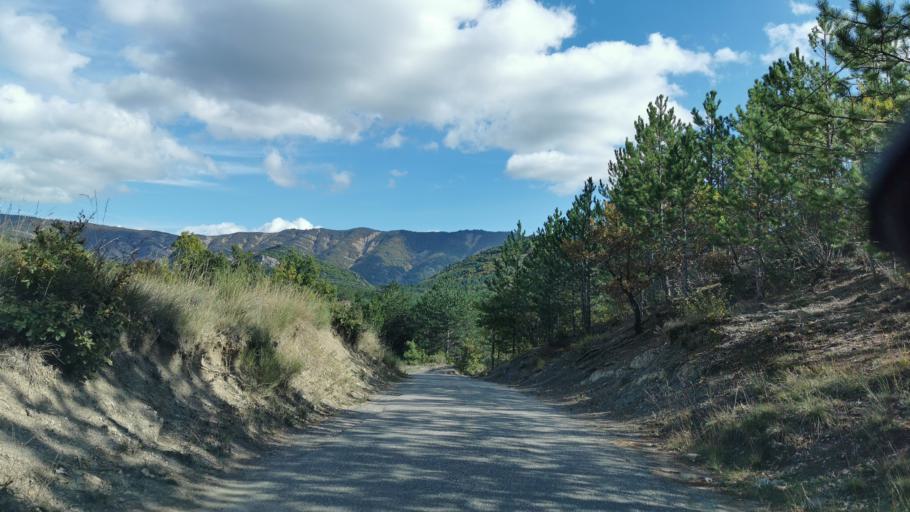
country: FR
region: Provence-Alpes-Cote d'Azur
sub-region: Departement des Alpes-de-Haute-Provence
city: Sisteron
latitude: 44.1856
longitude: 6.0175
